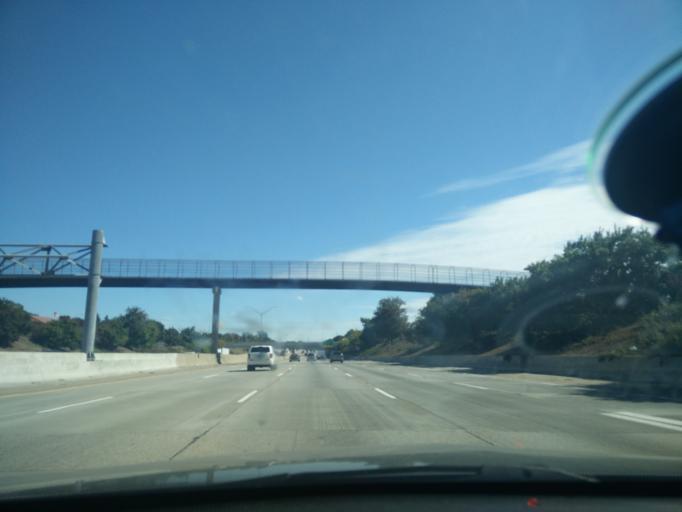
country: US
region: Michigan
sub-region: Oakland County
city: Madison Heights
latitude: 42.4909
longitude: -83.0721
